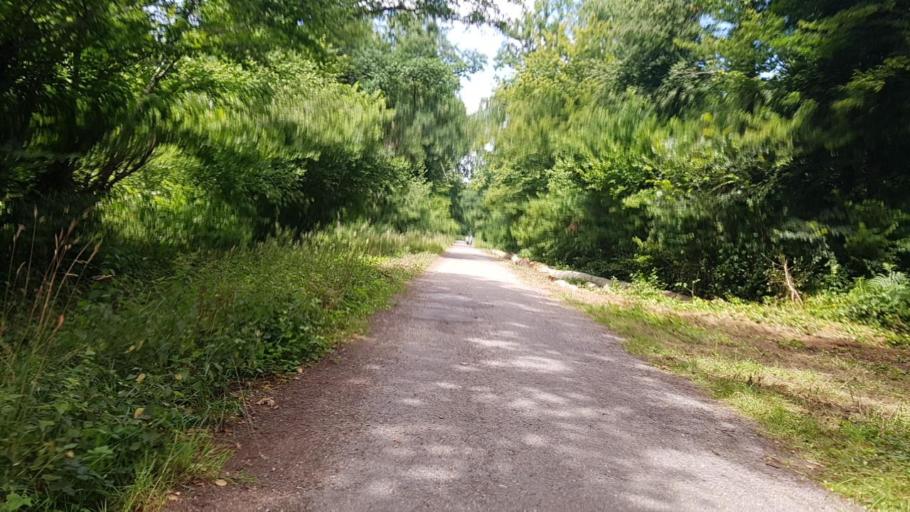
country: FR
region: Picardie
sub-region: Departement de l'Oise
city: Montmacq
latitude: 49.4743
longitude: 2.9182
